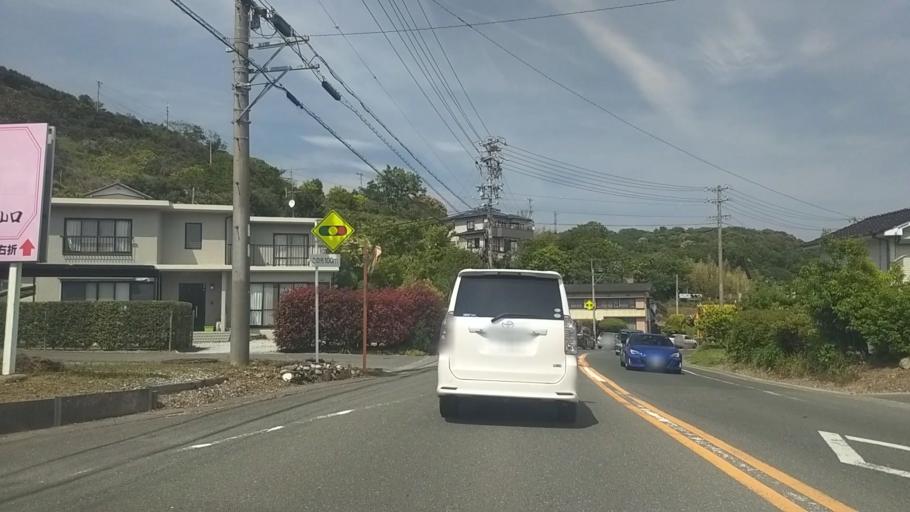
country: JP
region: Shizuoka
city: Kosai-shi
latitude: 34.7907
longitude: 137.6126
